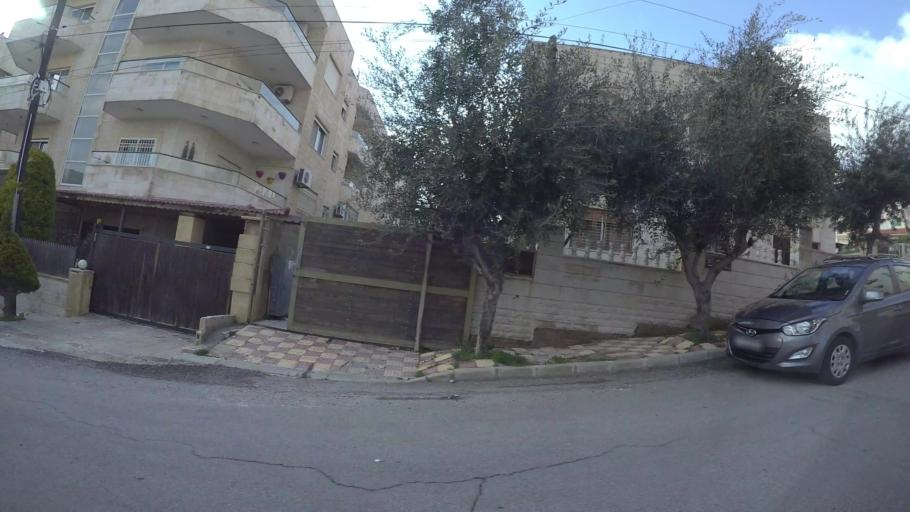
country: JO
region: Amman
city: Al Jubayhah
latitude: 31.9875
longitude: 35.8534
